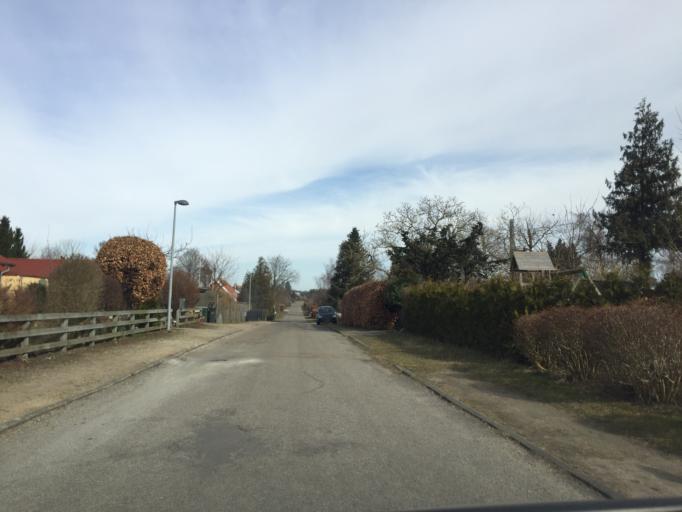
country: DK
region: Capital Region
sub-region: Fureso Kommune
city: Farum
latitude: 55.8128
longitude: 12.3639
